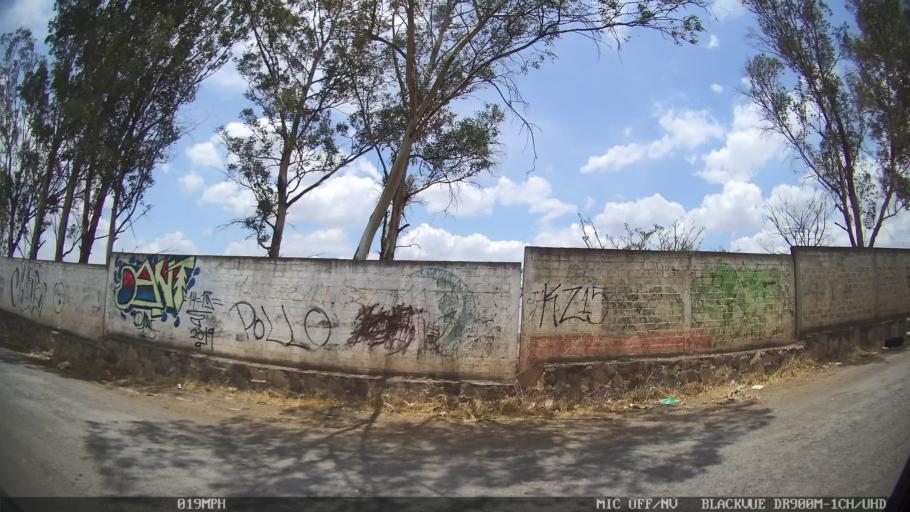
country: MX
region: Jalisco
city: Tonala
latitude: 20.6308
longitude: -103.2225
